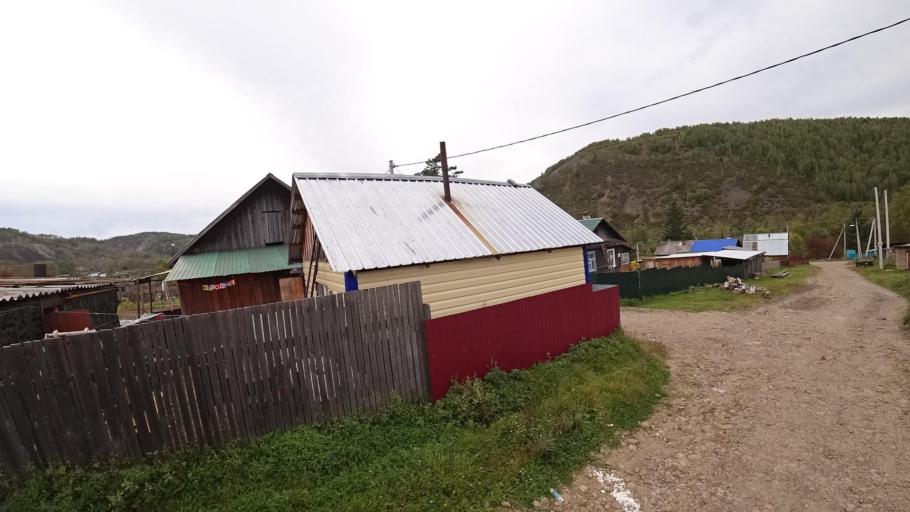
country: RU
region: Jewish Autonomous Oblast
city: Khingansk
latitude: 49.1303
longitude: 131.2009
